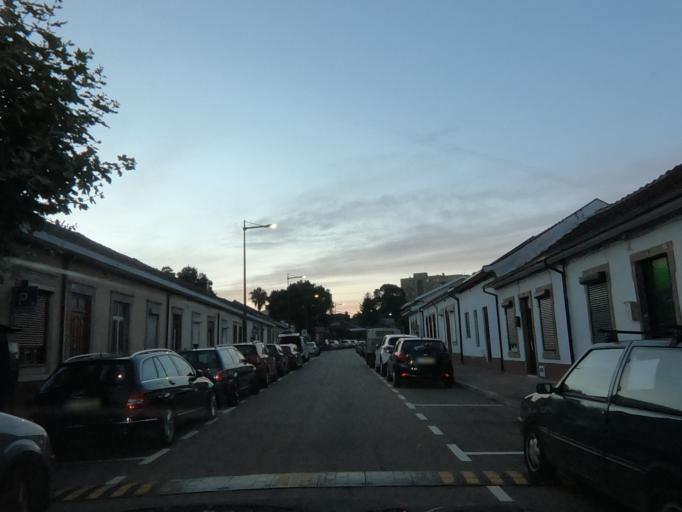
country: PT
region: Porto
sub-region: Valongo
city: Valongo
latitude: 41.1906
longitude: -8.5000
